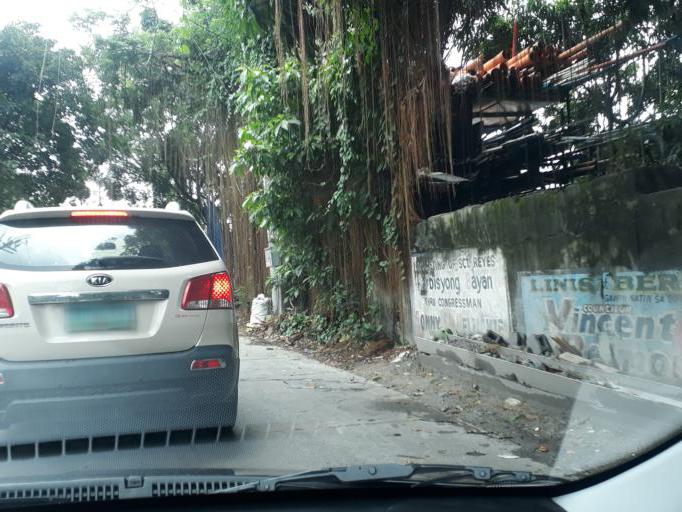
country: PH
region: Calabarzon
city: Del Monte
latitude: 14.6272
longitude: 121.0248
